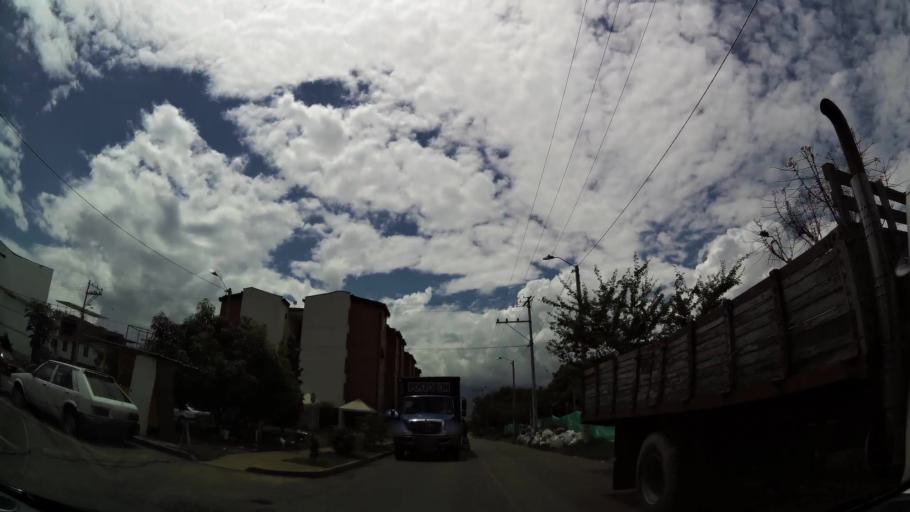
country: CO
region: Valle del Cauca
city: Cali
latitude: 3.3805
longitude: -76.5091
